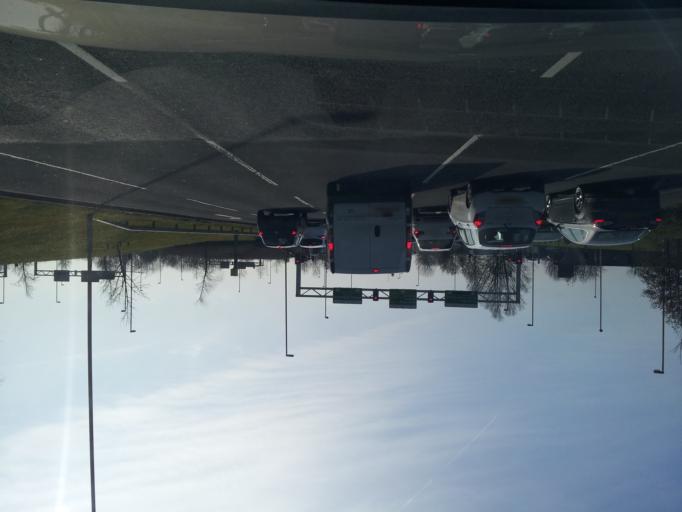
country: GB
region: England
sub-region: Leicestershire
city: Enderby
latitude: 52.5966
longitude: -1.1852
